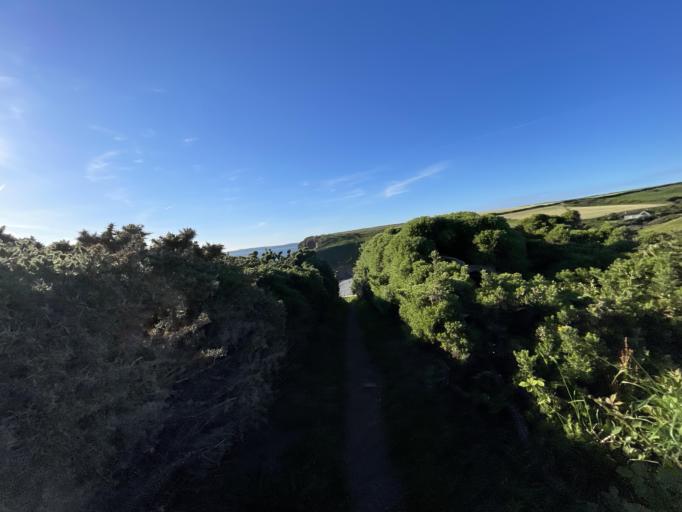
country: GB
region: Wales
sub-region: Pembrokeshire
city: Herbrandston
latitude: 51.8113
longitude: -5.1028
